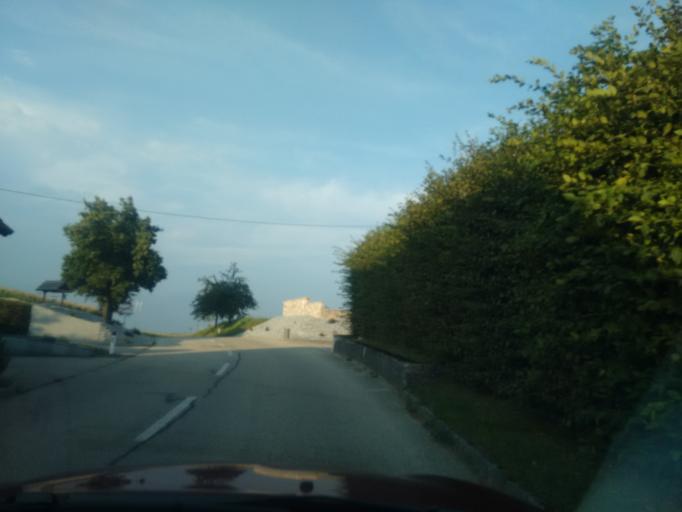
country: AT
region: Upper Austria
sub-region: Wels-Land
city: Offenhausen
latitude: 48.1577
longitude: 13.8028
